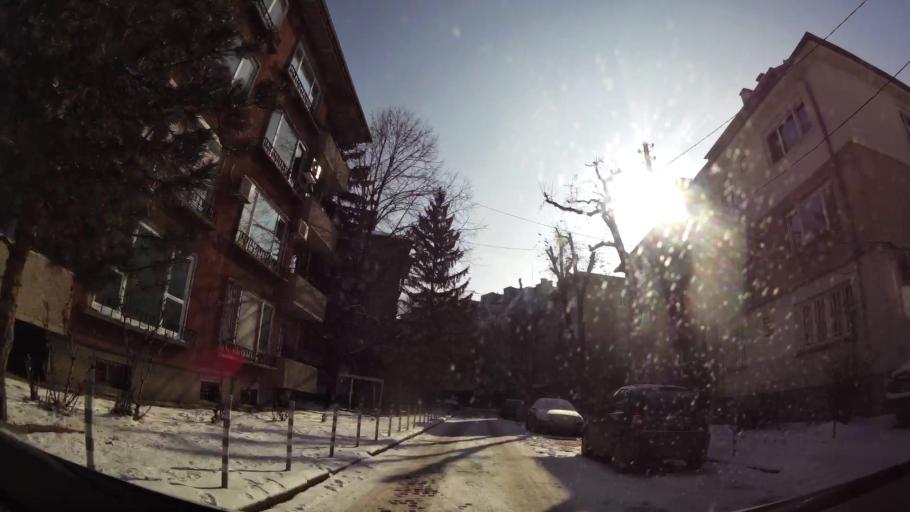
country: BG
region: Sofia-Capital
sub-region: Stolichna Obshtina
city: Sofia
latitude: 42.6819
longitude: 23.3264
